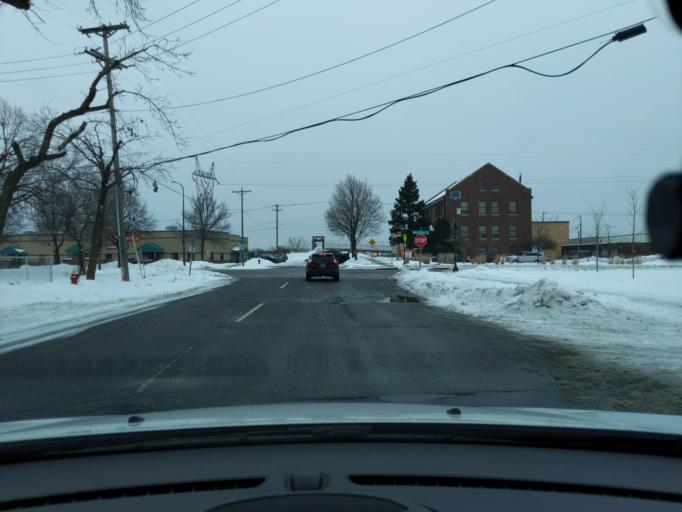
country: US
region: Minnesota
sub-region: Ramsey County
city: Falcon Heights
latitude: 44.9674
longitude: -93.1568
